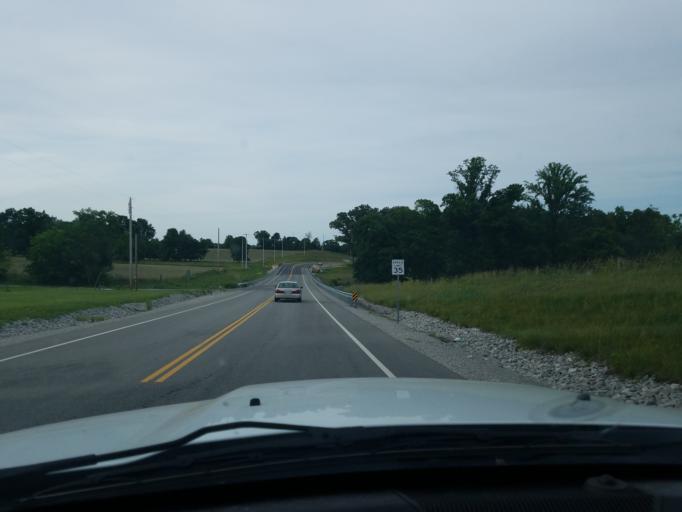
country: US
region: Tennessee
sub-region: Putnam County
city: Baxter
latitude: 36.1312
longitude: -85.5812
